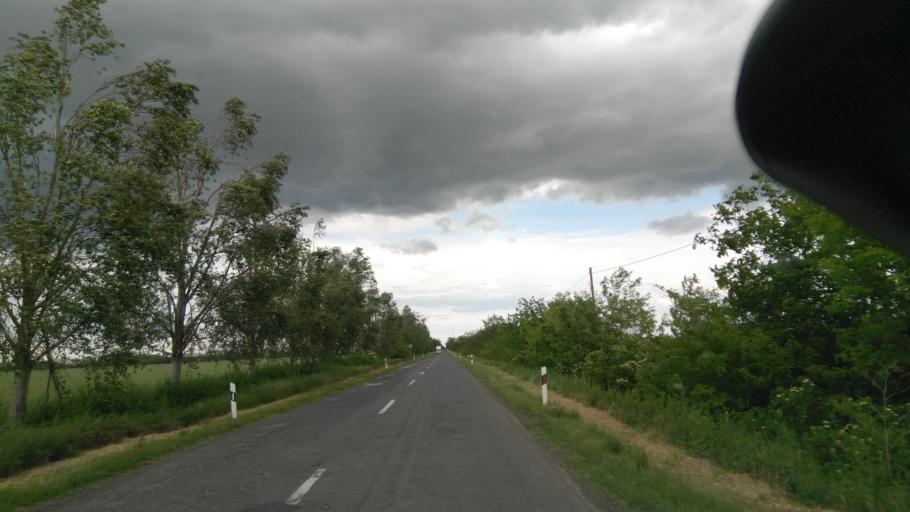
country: HU
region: Bekes
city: Gadoros
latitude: 46.6716
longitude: 20.6145
